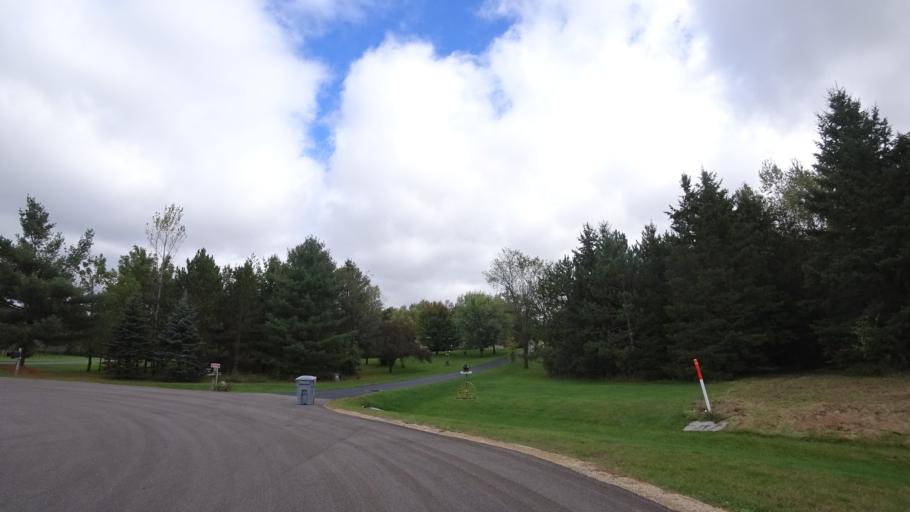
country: US
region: Wisconsin
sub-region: Saint Croix County
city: Woodville
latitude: 44.9255
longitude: -92.2750
